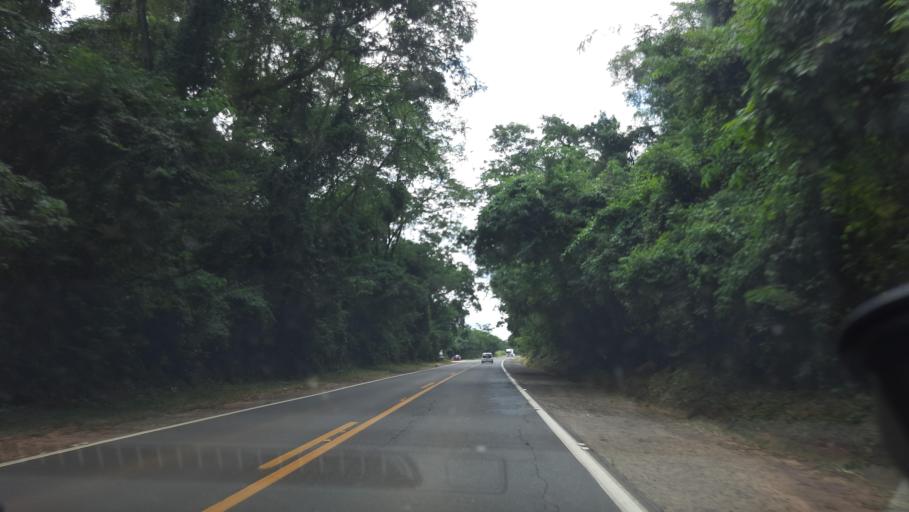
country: BR
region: Sao Paulo
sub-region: Mococa
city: Mococa
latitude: -21.4924
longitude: -47.0738
